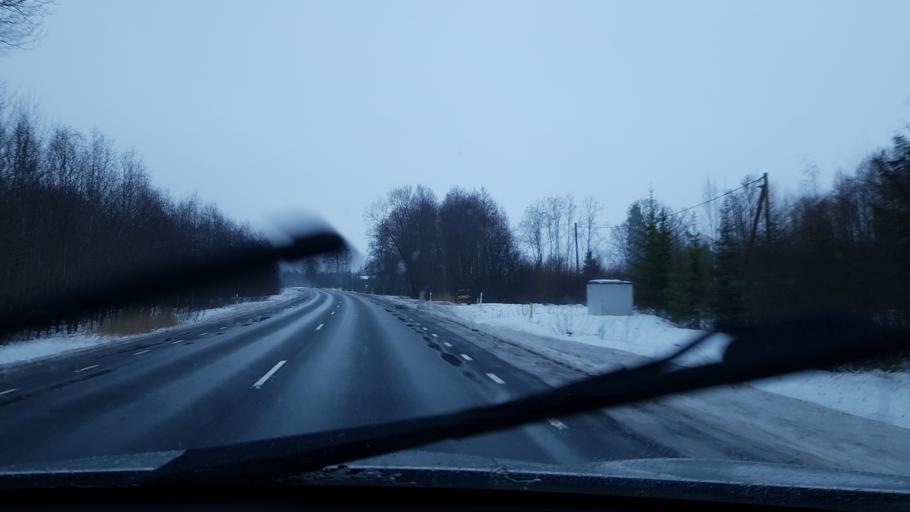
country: EE
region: Jaervamaa
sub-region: Tueri vald
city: Sarevere
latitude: 58.8006
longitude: 25.2354
